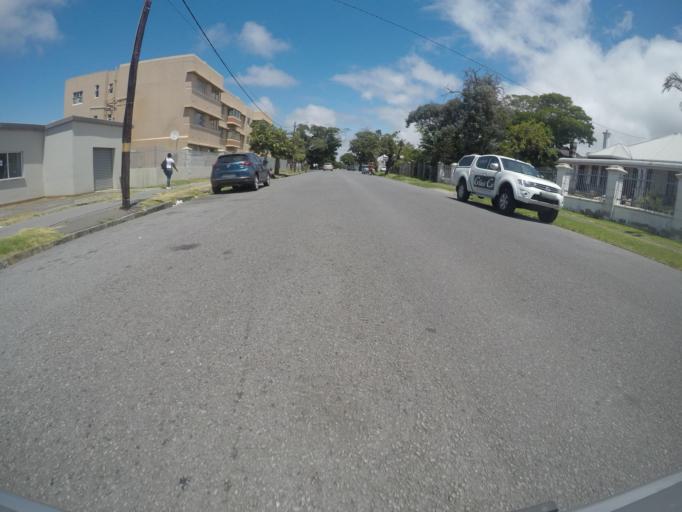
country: ZA
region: Eastern Cape
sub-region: Buffalo City Metropolitan Municipality
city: East London
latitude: -32.9992
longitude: 27.8999
